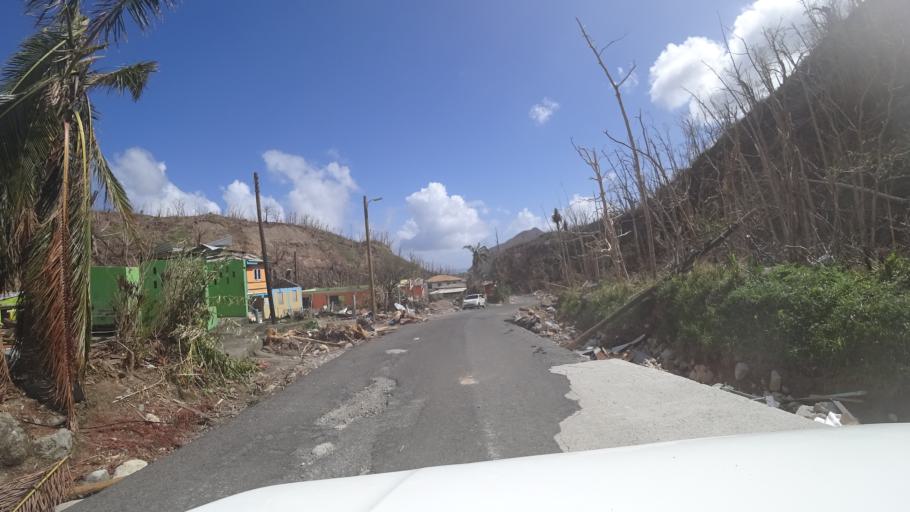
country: DM
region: Saint Patrick
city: Berekua
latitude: 15.2611
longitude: -61.3186
